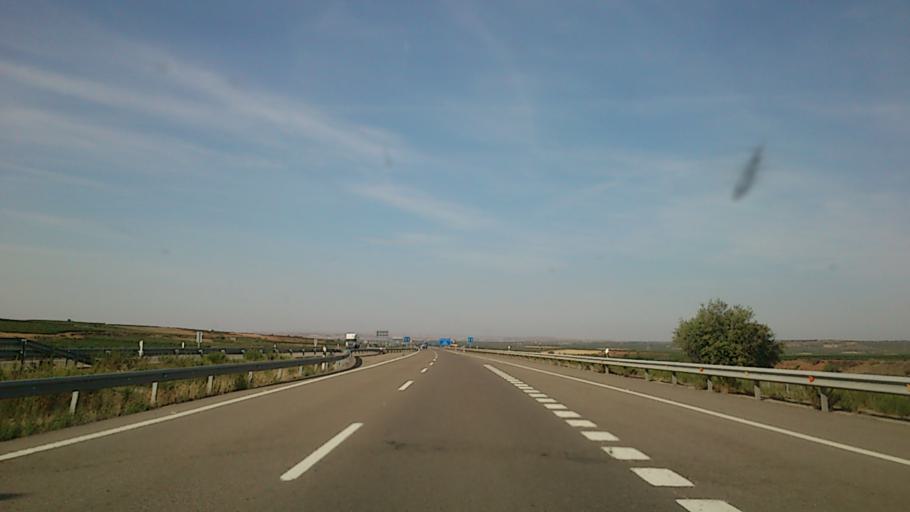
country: ES
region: Aragon
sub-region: Provincia de Zaragoza
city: Paniza
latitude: 41.3039
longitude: -1.2128
